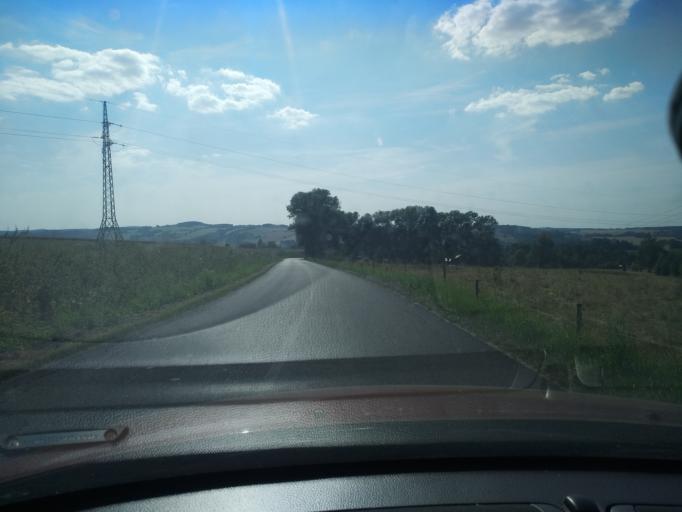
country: PL
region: Lower Silesian Voivodeship
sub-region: Powiat lubanski
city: Lesna
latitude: 51.0265
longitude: 15.2848
